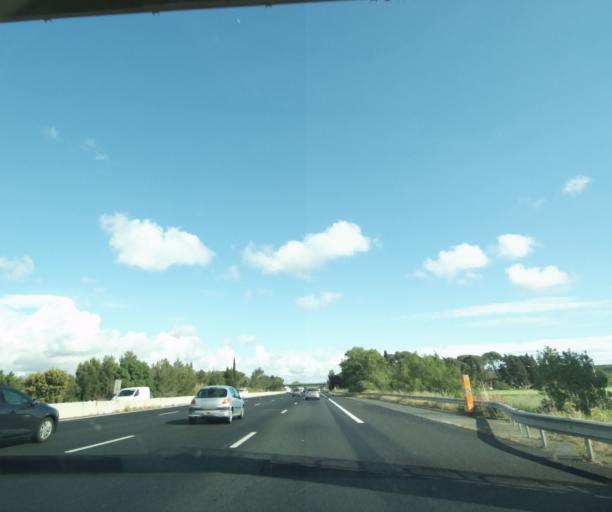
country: FR
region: Provence-Alpes-Cote d'Azur
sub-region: Departement des Bouches-du-Rhone
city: Pelissanne
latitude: 43.6148
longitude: 5.1418
